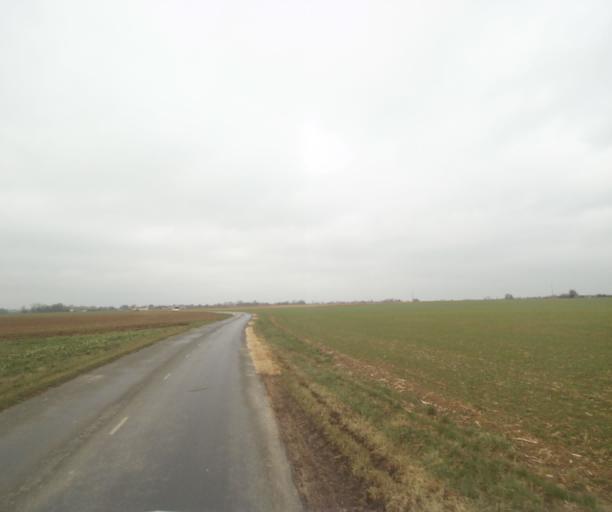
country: FR
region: Champagne-Ardenne
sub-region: Departement de la Haute-Marne
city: Villiers-en-Lieu
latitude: 48.6874
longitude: 4.8166
